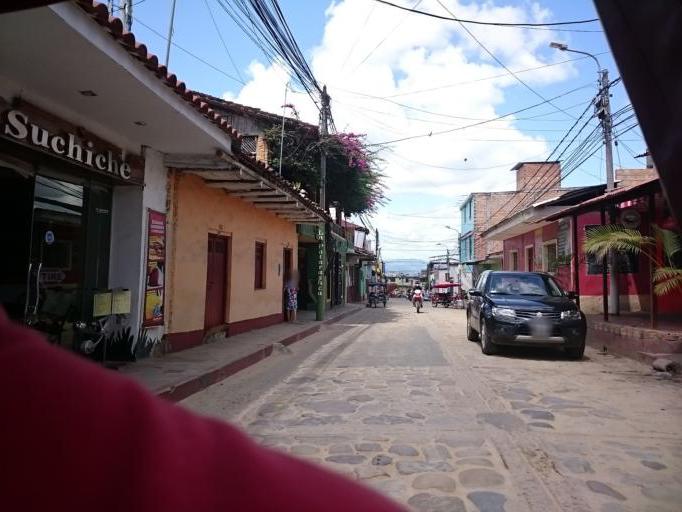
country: PE
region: San Martin
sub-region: Provincia de San Martin
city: Tarapoto
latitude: -6.4869
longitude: -76.3578
